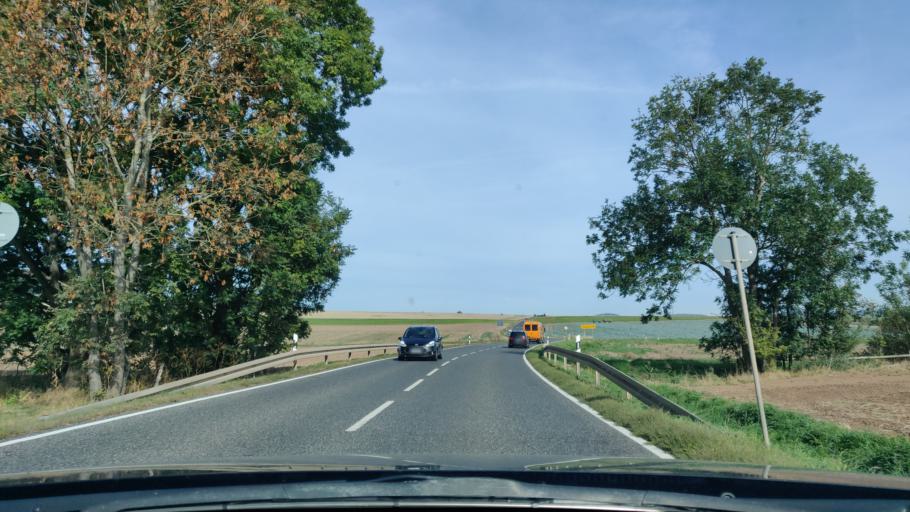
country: DE
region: Hesse
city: Fritzlar
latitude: 51.1637
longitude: 9.2704
